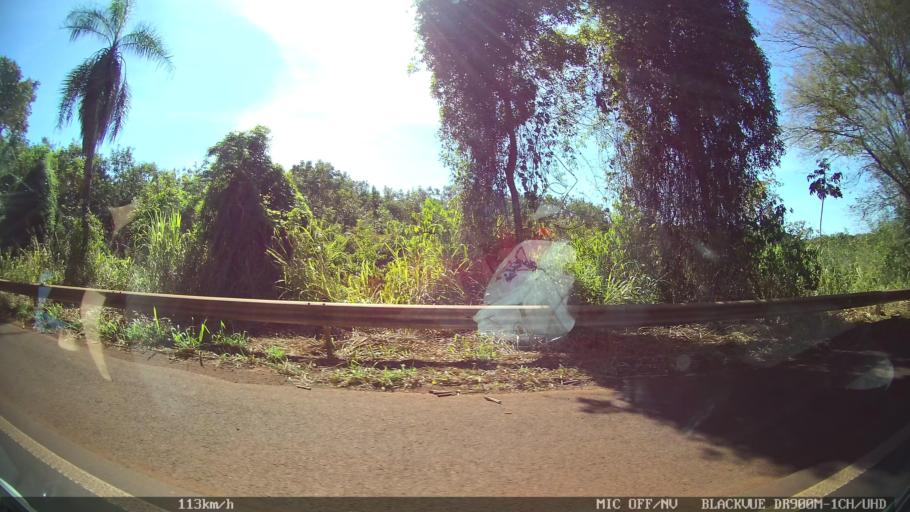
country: BR
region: Sao Paulo
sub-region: Guaira
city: Guaira
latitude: -20.4434
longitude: -48.3285
